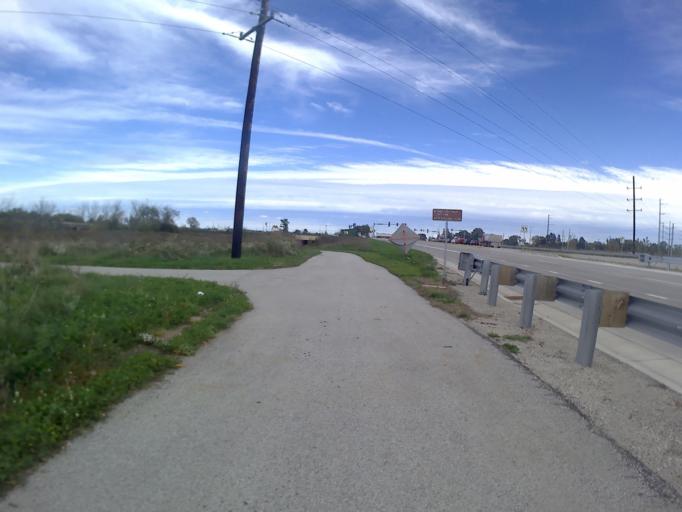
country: US
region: Illinois
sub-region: Kane County
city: South Elgin
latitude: 41.9781
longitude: -88.2717
